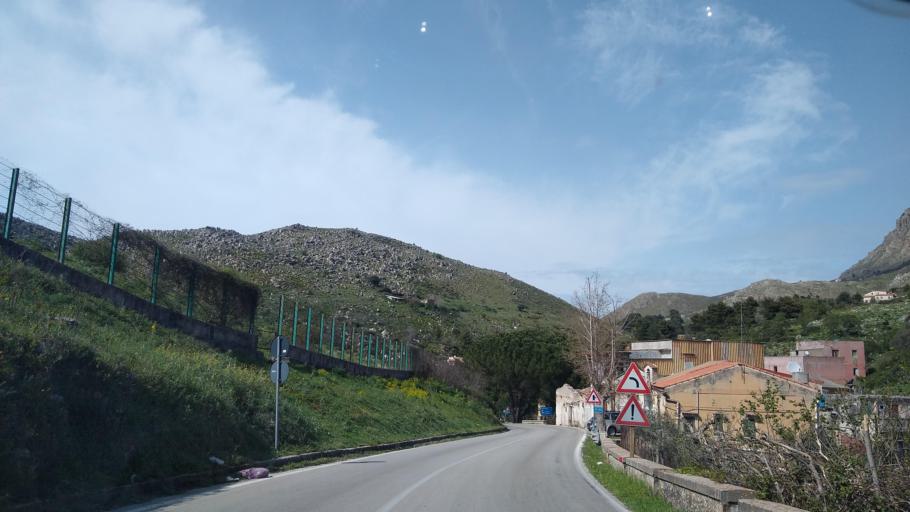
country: IT
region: Sicily
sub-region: Palermo
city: Pioppo
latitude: 38.0470
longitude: 13.1979
